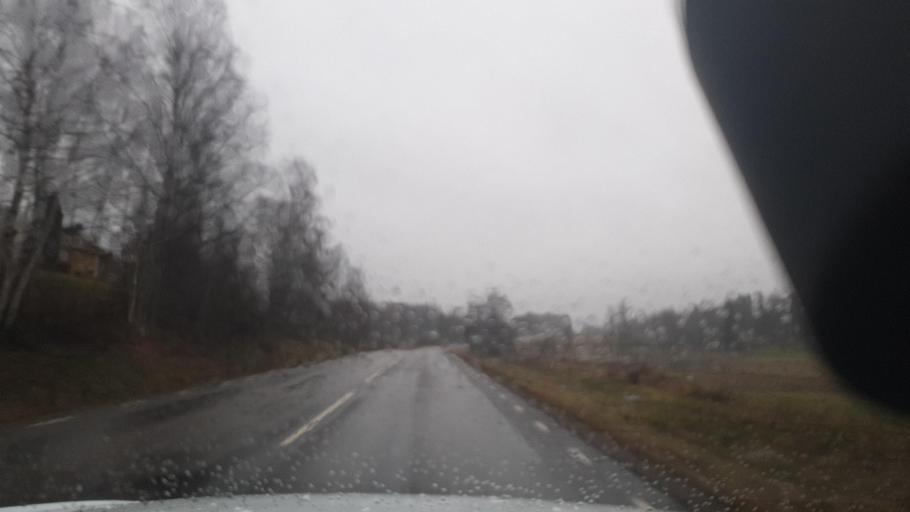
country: SE
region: Vaermland
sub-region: Arvika Kommun
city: Arvika
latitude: 59.7005
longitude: 12.6368
